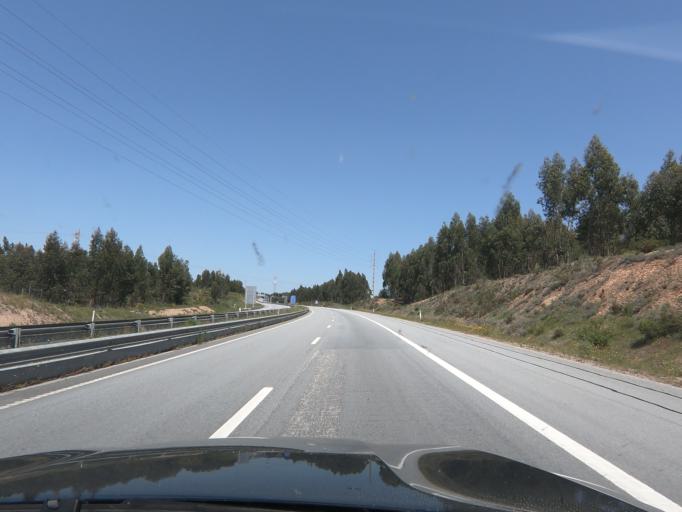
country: PT
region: Santarem
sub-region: Chamusca
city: Vila Nova da Barquinha
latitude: 39.5045
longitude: -8.4265
